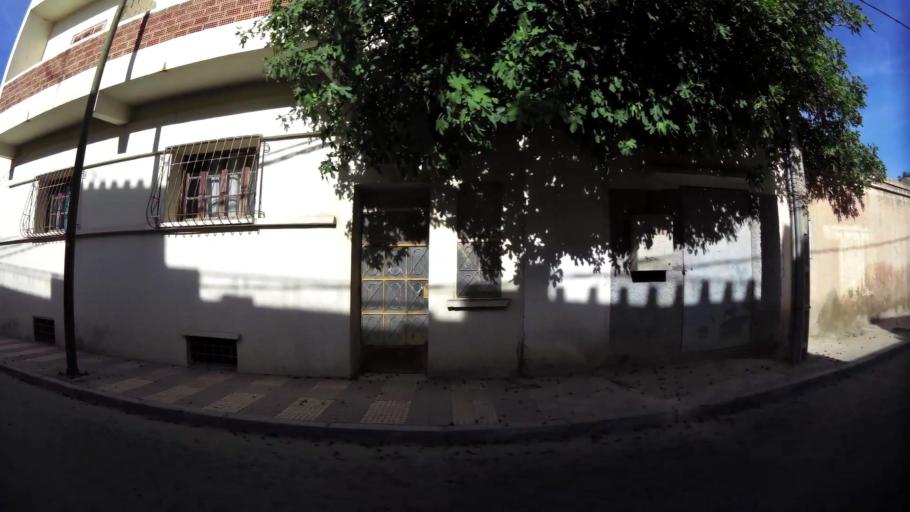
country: MA
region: Oriental
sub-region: Oujda-Angad
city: Oujda
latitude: 34.6744
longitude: -1.9082
